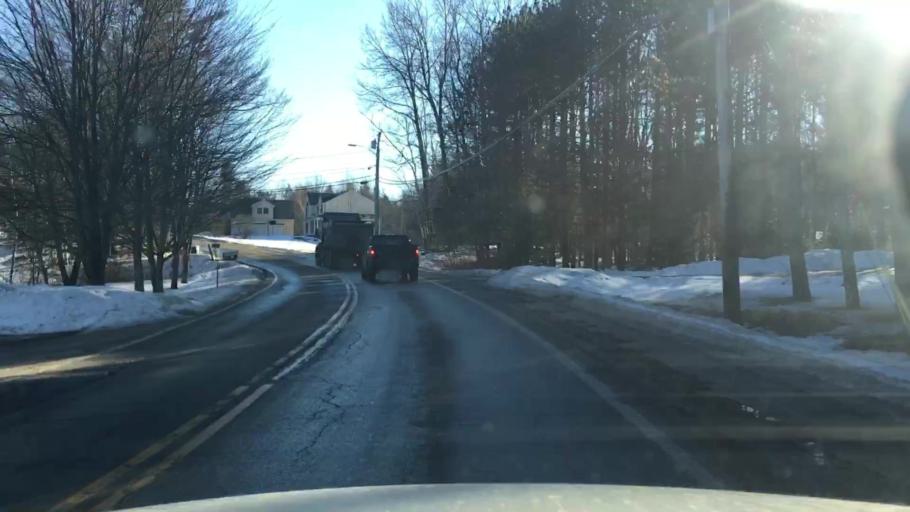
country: US
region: Maine
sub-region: Cumberland County
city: Westbrook
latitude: 43.7145
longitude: -70.3597
